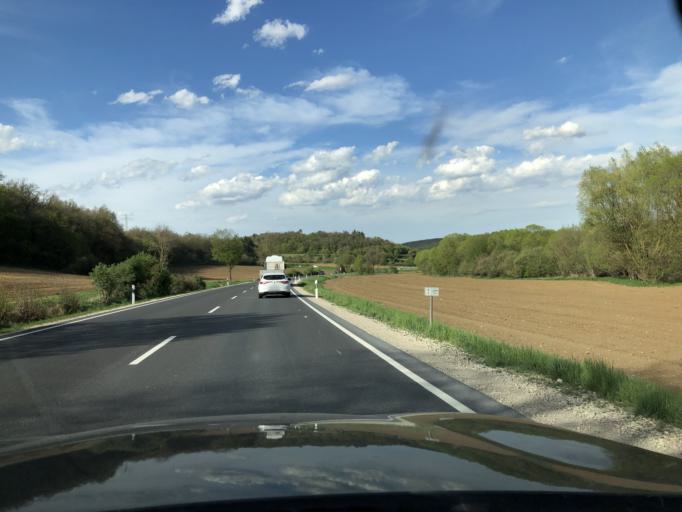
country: DE
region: Bavaria
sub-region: Regierungsbezirk Mittelfranken
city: Treuchtlingen
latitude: 48.9331
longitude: 10.9199
